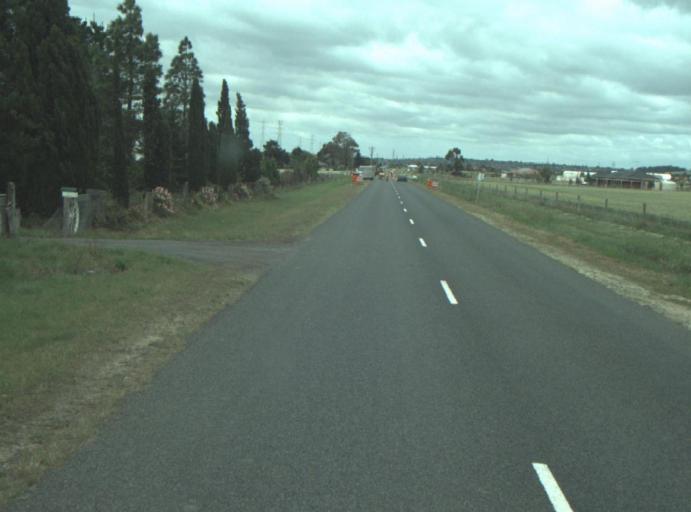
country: AU
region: Victoria
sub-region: Greater Geelong
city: Bell Post Hill
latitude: -38.0553
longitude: 144.3423
